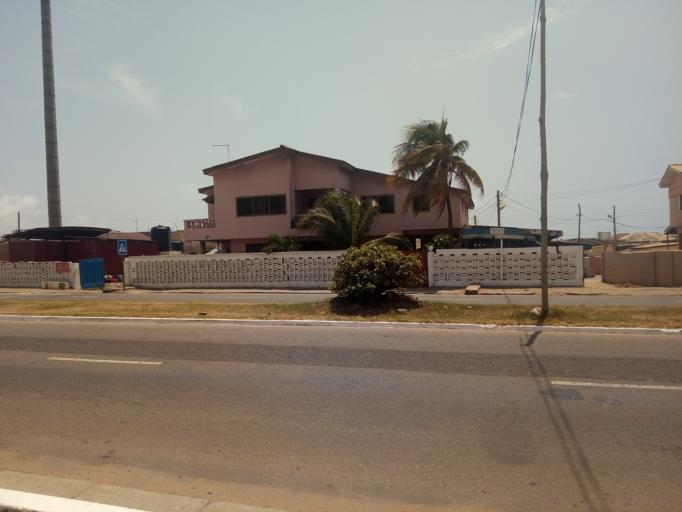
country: GH
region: Greater Accra
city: Accra
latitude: 5.5507
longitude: -0.1909
